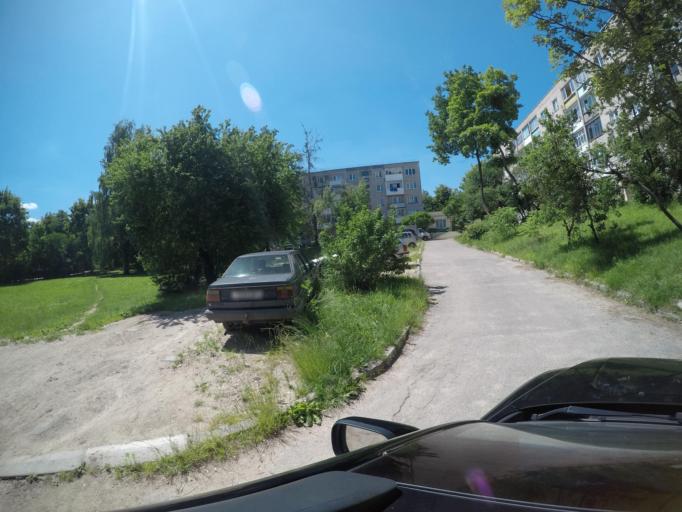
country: BY
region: Grodnenskaya
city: Hrodna
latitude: 53.6976
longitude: 23.8107
